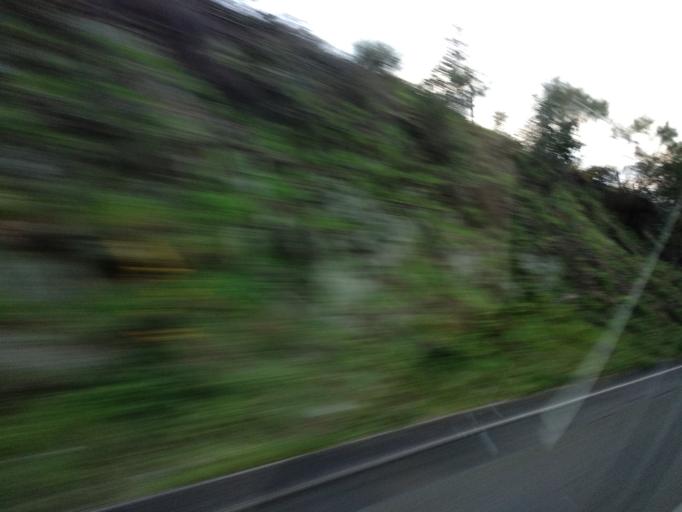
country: PT
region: Braga
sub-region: Braga
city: Oliveira
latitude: 41.4907
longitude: -8.4652
